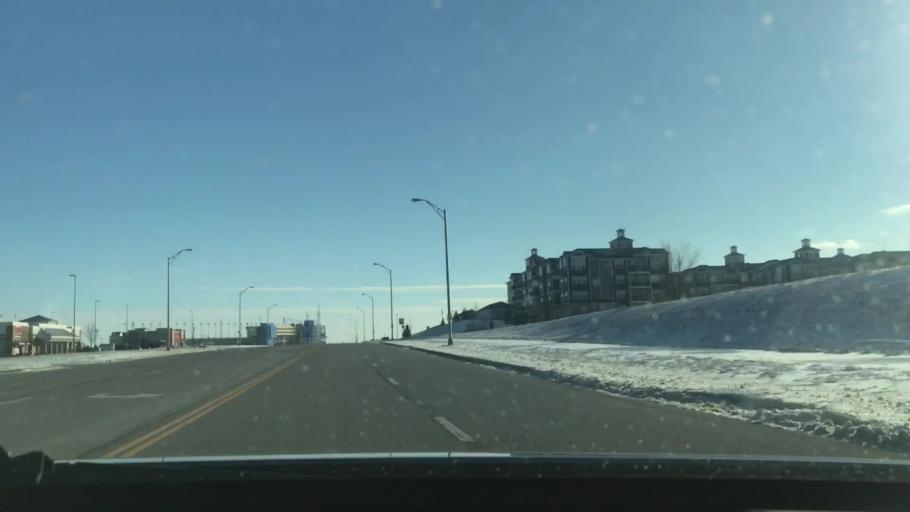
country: US
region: Kansas
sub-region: Wyandotte County
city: Edwardsville
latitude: 39.1284
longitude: -94.8353
